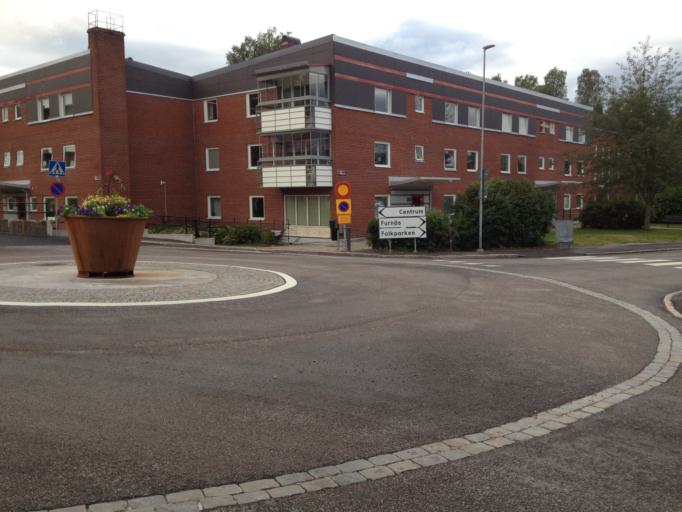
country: SE
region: Vaestra Goetaland
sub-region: Bengtsfors Kommun
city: Bengtsfors
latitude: 59.0308
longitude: 12.2213
